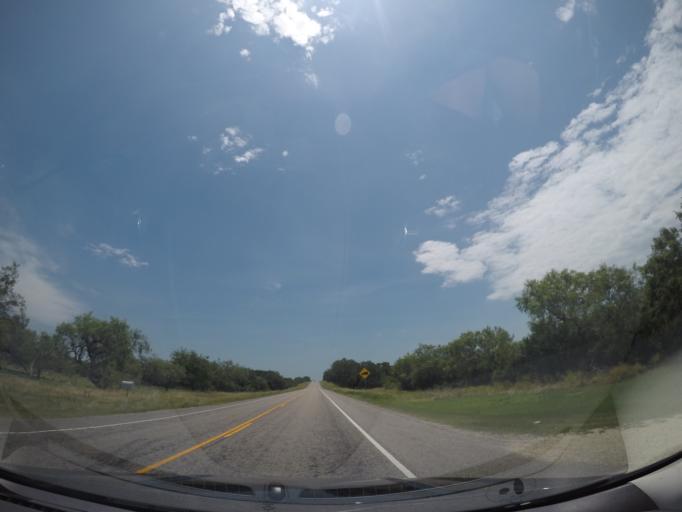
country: US
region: Texas
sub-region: Uvalde County
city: Uvalde Estates
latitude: 29.2429
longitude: -100.0756
